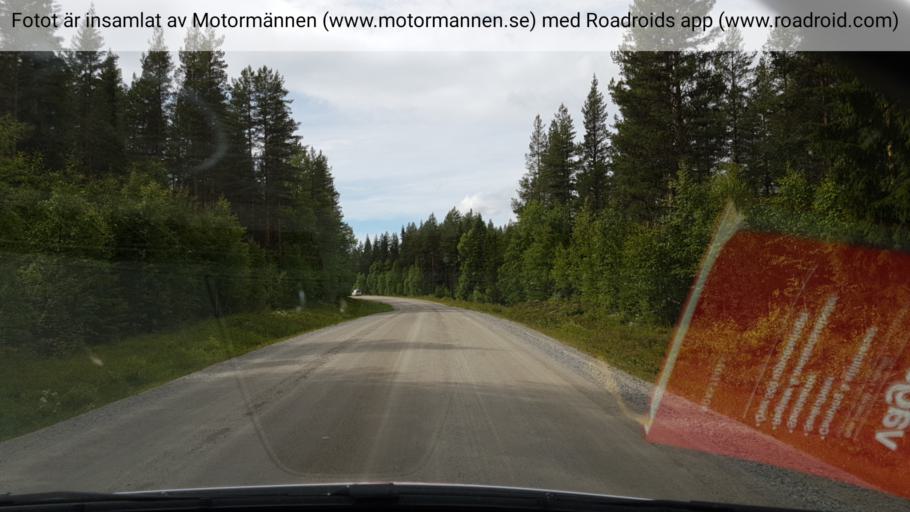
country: SE
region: Vaesternorrland
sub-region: Solleftea Kommun
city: Solleftea
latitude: 63.3207
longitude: 17.3288
